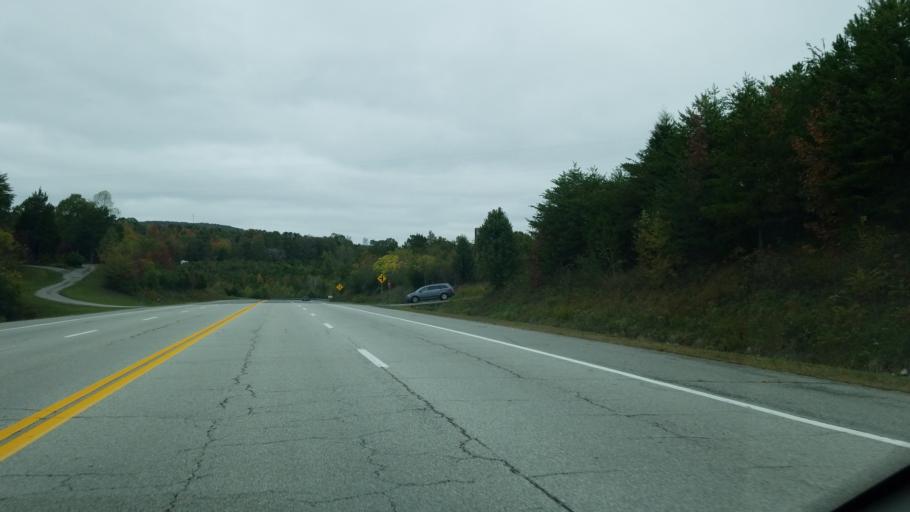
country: US
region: Tennessee
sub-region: Rhea County
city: Dayton
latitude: 35.4673
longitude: -85.0201
